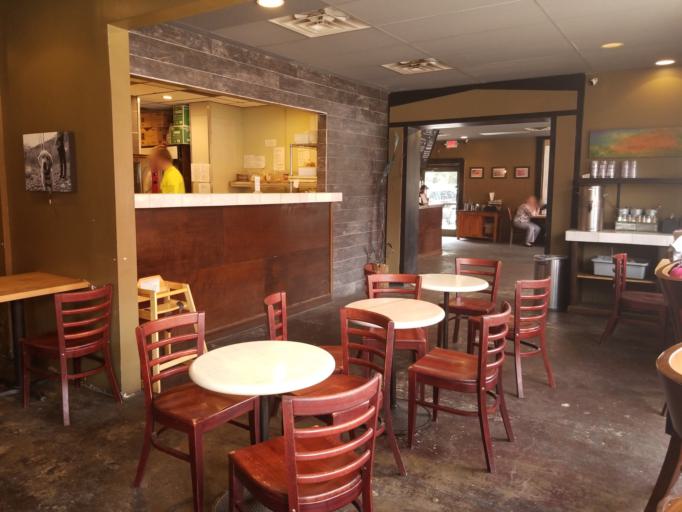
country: US
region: Nebraska
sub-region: Lancaster County
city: Lincoln
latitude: 40.8394
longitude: -96.6540
